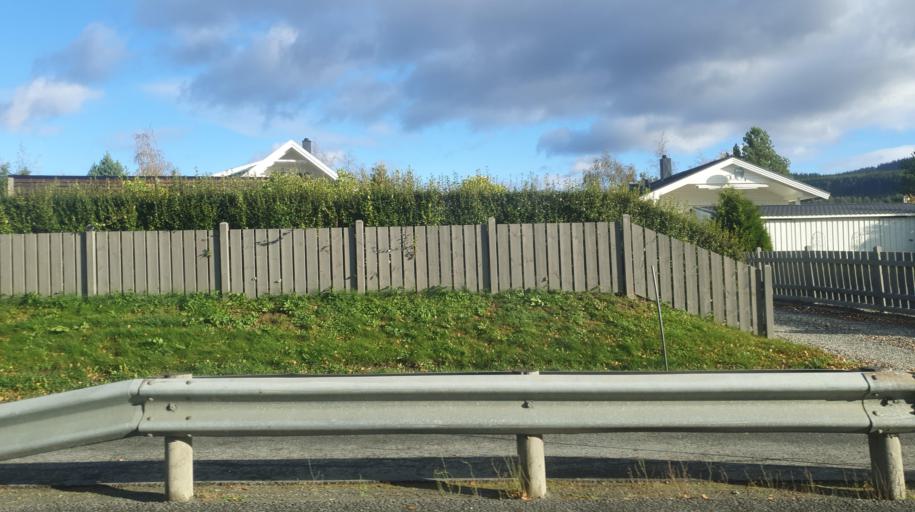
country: NO
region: Sor-Trondelag
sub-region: Klaebu
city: Klaebu
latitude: 63.3001
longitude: 10.4722
